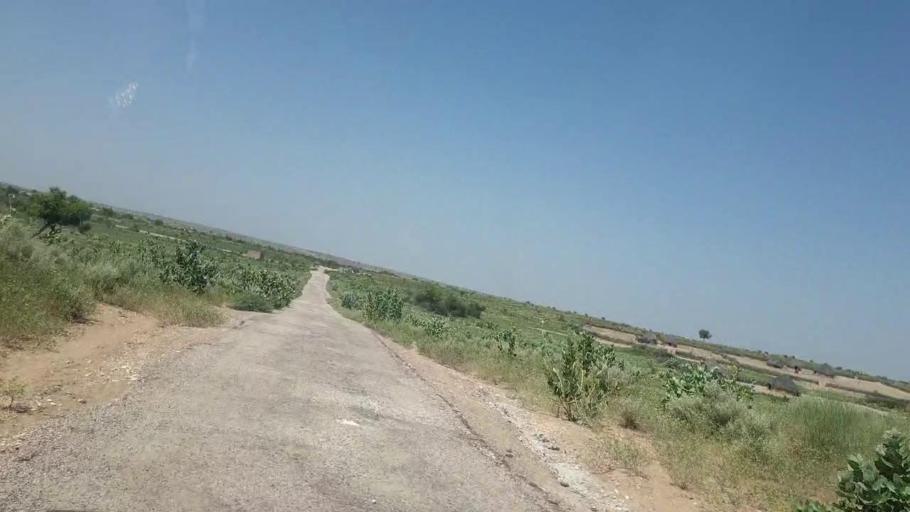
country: PK
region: Sindh
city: Chor
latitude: 25.3591
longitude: 70.3300
